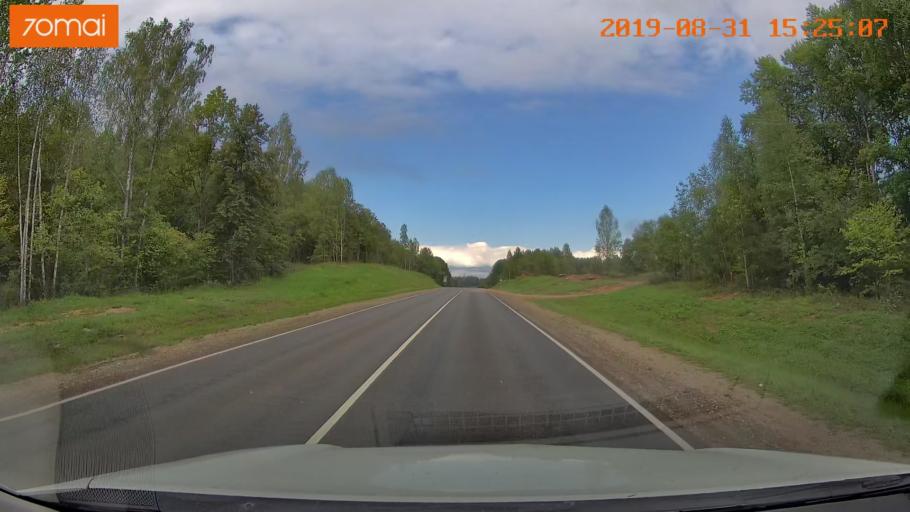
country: RU
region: Kaluga
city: Baryatino
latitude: 54.5370
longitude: 34.5148
